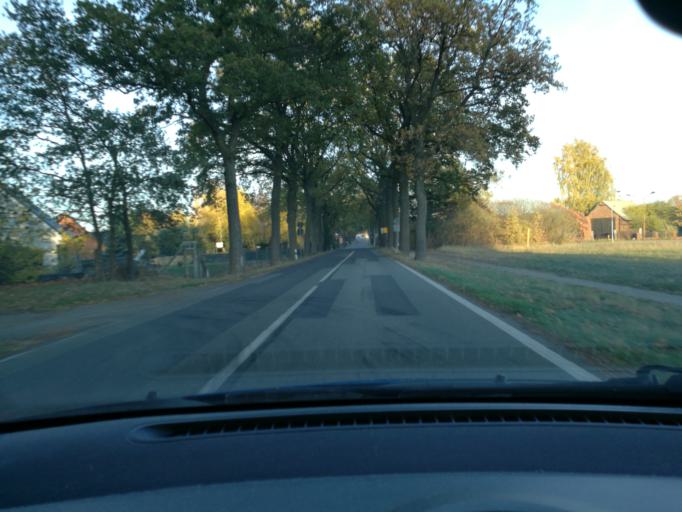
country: DE
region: Brandenburg
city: Perleberg
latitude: 53.0838
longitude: 11.8897
